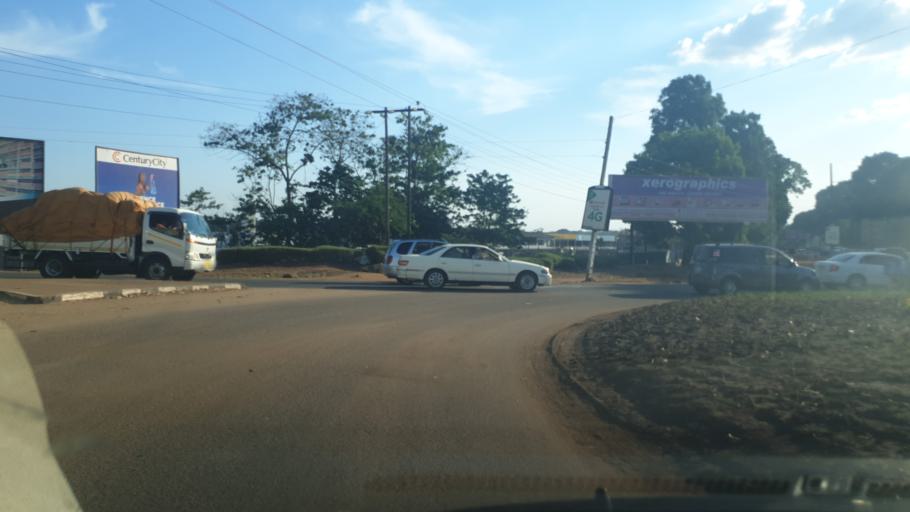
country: MW
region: Central Region
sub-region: Lilongwe District
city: Lilongwe
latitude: -13.9758
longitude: 33.7792
